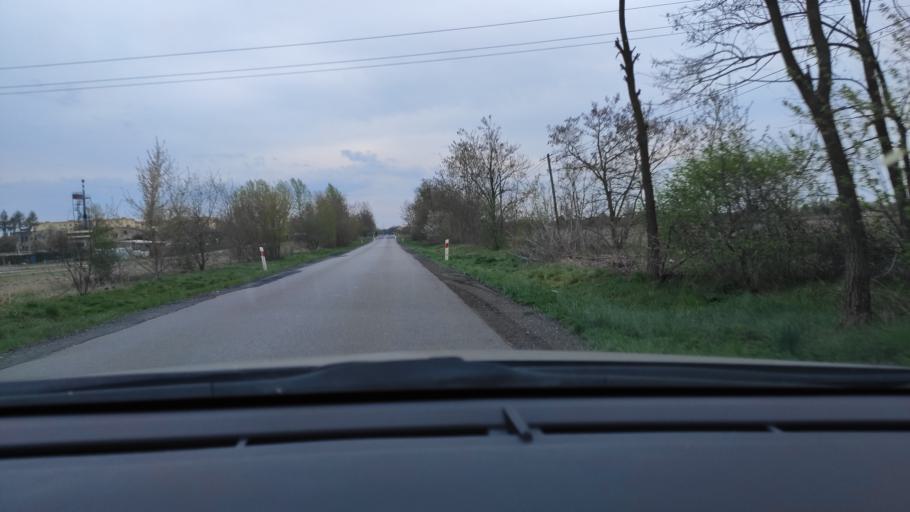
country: PL
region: Masovian Voivodeship
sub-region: Powiat zwolenski
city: Zwolen
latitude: 51.3663
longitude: 21.5642
